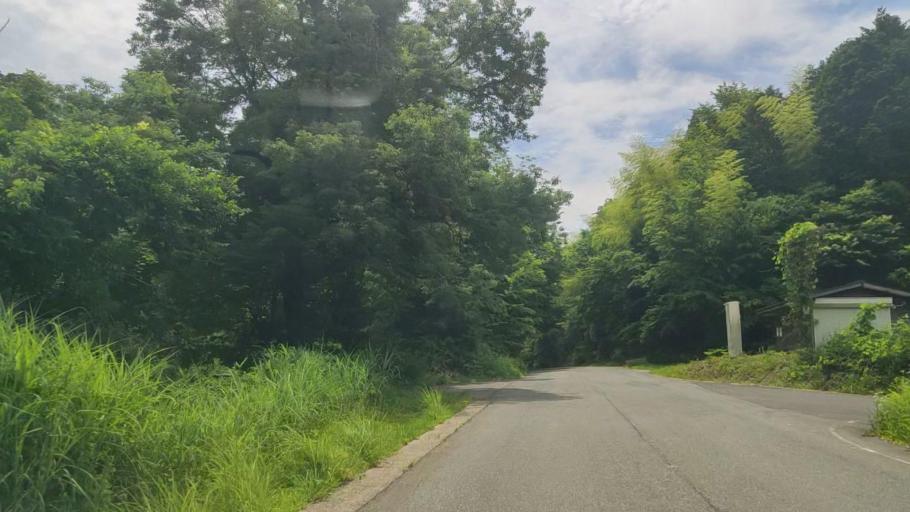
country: JP
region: Hyogo
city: Toyooka
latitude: 35.5049
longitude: 134.6870
